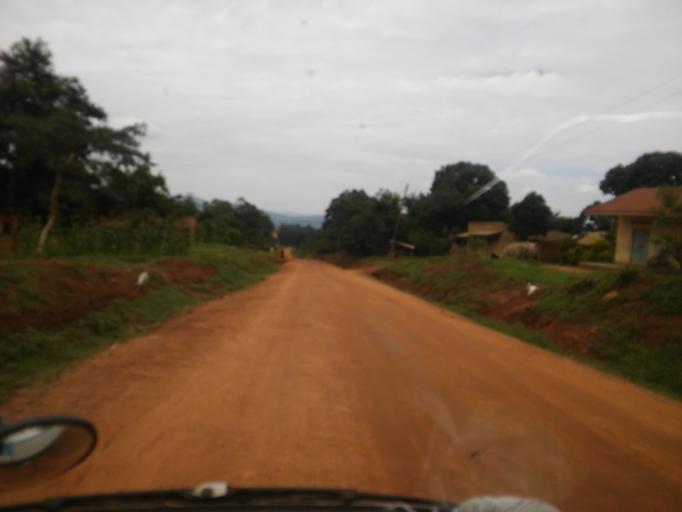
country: UG
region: Eastern Region
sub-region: Mbale District
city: Mbale
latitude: 0.9799
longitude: 34.2035
